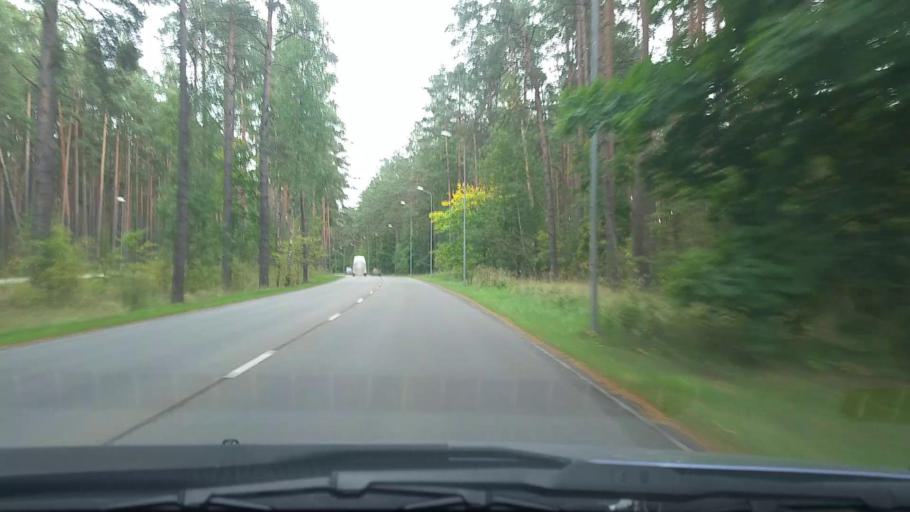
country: LV
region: Riga
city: Jaunciems
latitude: 56.9770
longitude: 24.2176
